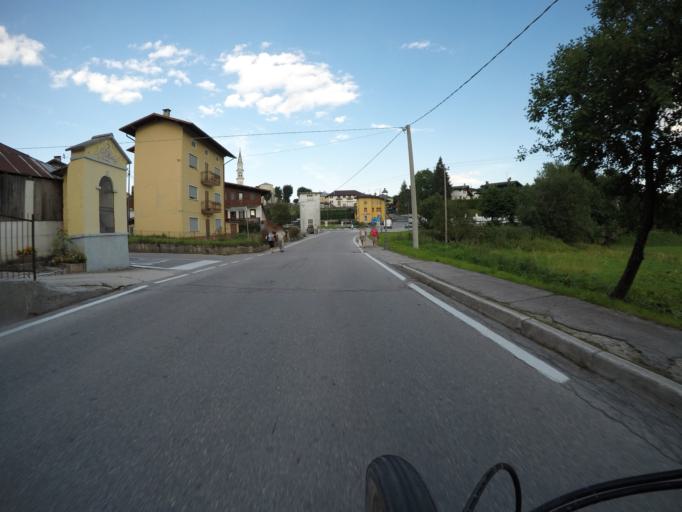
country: IT
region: Veneto
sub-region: Provincia di Vicenza
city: Gallio
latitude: 45.8930
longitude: 11.5434
